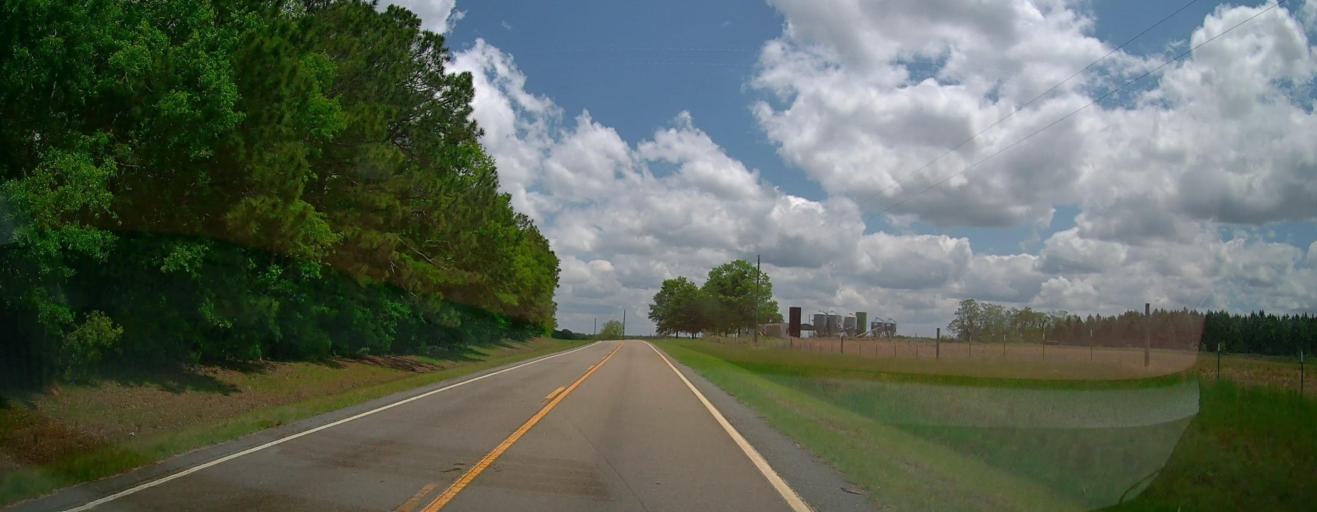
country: US
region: Georgia
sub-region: Dodge County
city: Chester
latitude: 32.5409
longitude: -83.1870
